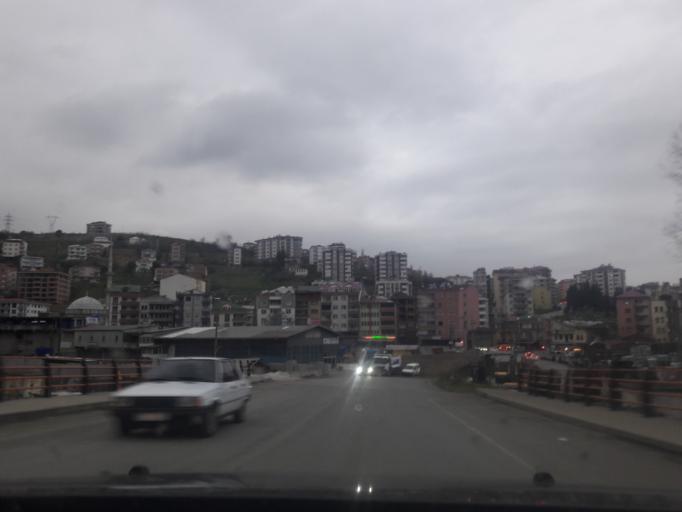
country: TR
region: Trabzon
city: Akcaabat
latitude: 41.0097
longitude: 39.5920
